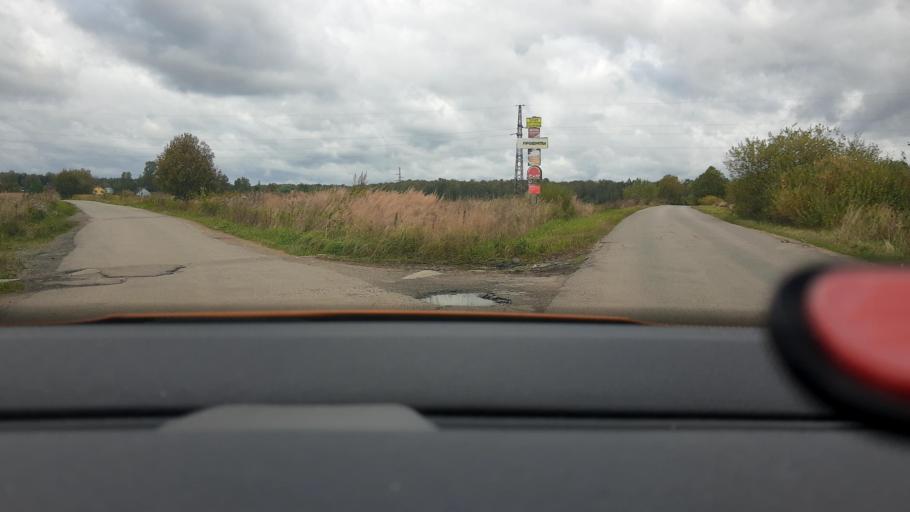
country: RU
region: Moskovskaya
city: Krasnoarmeysk
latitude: 56.0873
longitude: 38.0332
